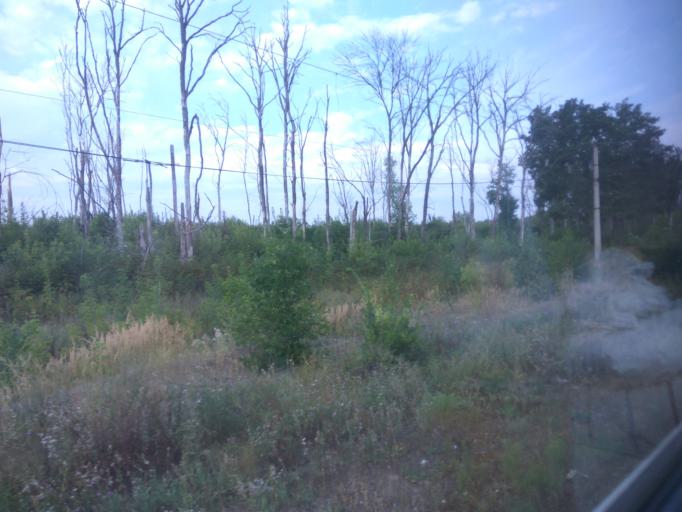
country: RU
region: Saratov
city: Rtishchevo
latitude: 52.2217
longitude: 43.8636
